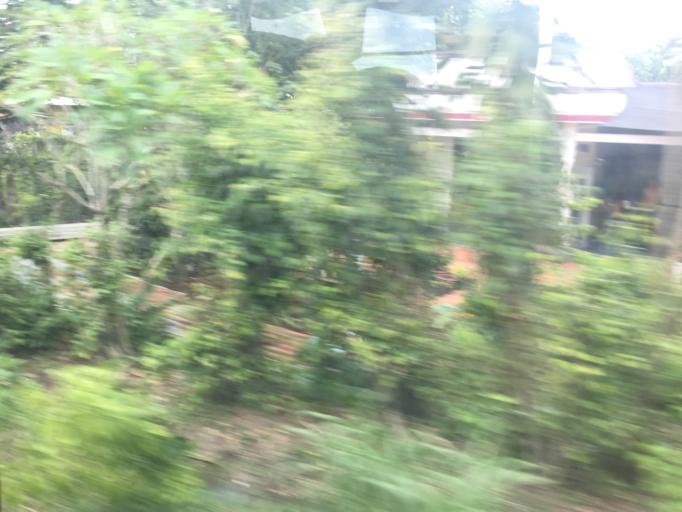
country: VN
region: Ho Chi Minh City
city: Cu Chi
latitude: 11.1203
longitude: 106.4786
